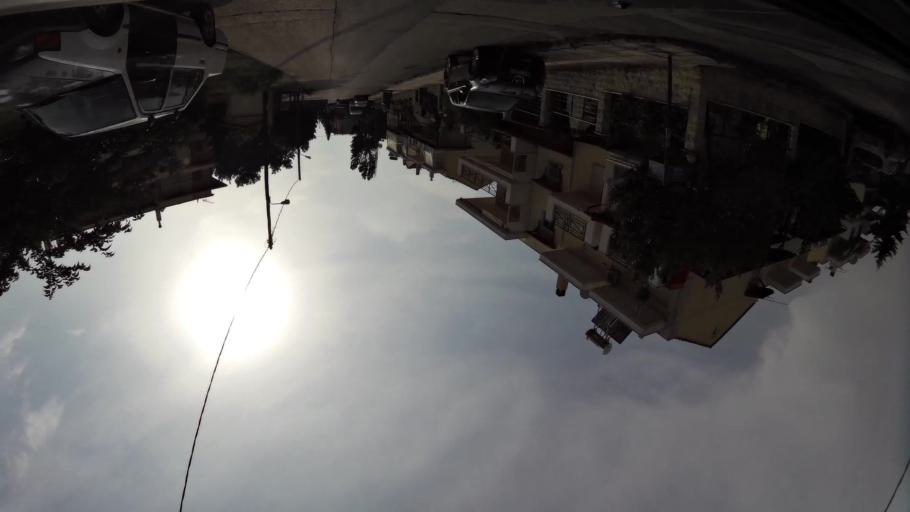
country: GR
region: Central Macedonia
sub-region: Nomos Thessalonikis
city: Oraiokastro
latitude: 40.7268
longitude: 22.9181
